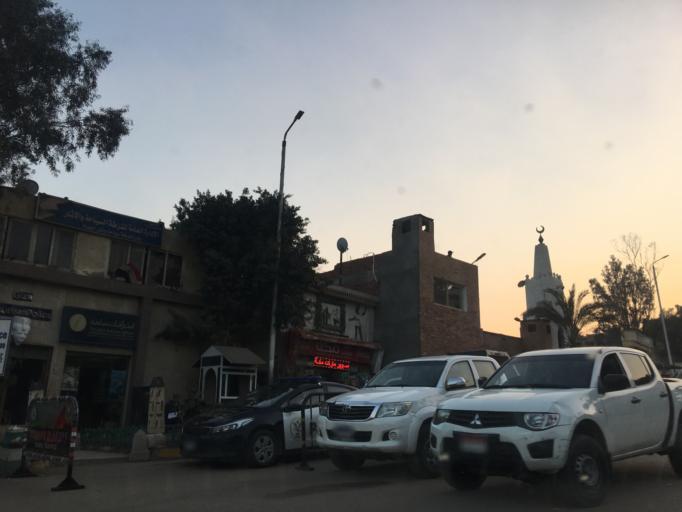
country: EG
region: Al Jizah
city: Al Jizah
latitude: 29.9839
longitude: 31.1336
